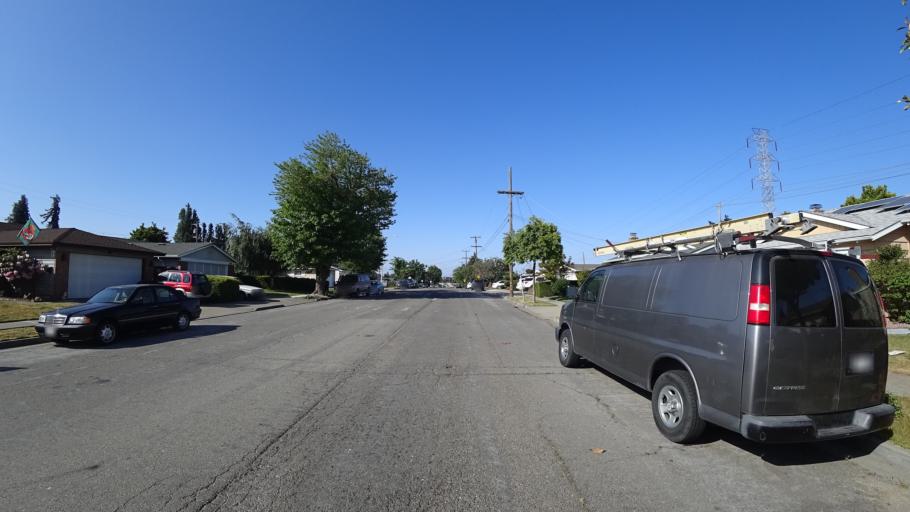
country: US
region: California
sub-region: Alameda County
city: Hayward
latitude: 37.6380
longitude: -122.0921
